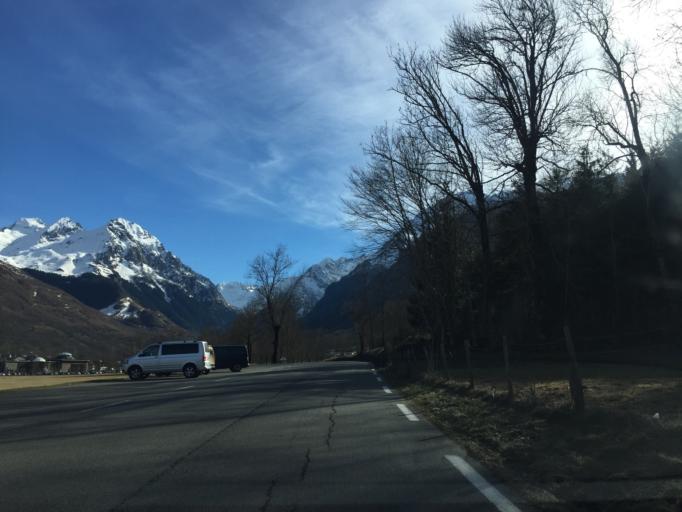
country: FR
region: Midi-Pyrenees
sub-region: Departement des Hautes-Pyrenees
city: Saint-Lary-Soulan
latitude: 42.8025
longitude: 0.4047
